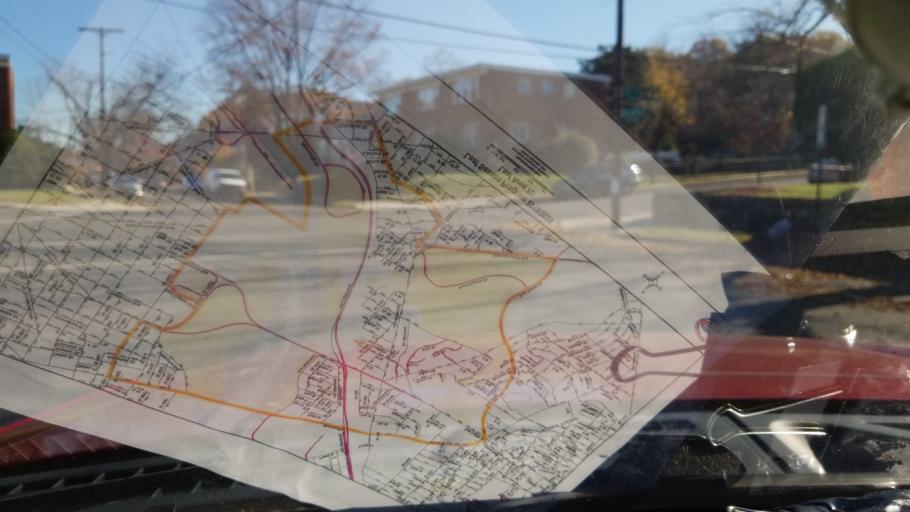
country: US
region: Maryland
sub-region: Prince George's County
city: Capitol Heights
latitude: 38.8929
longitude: -76.9479
